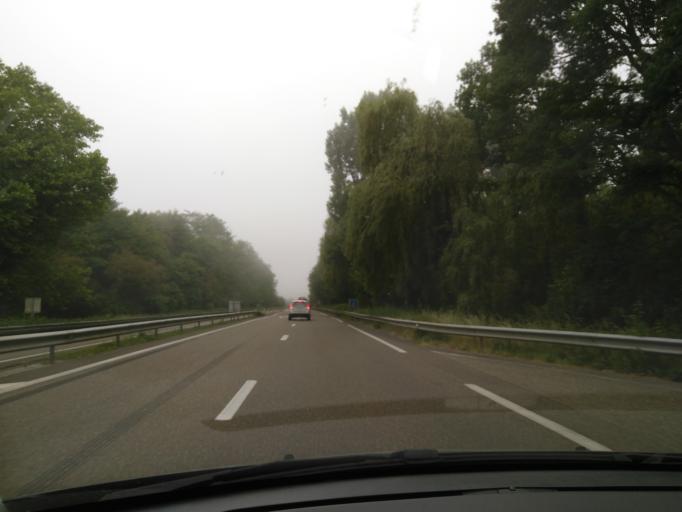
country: FR
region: Aquitaine
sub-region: Departement des Landes
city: Tartas
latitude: 43.8260
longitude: -0.8257
